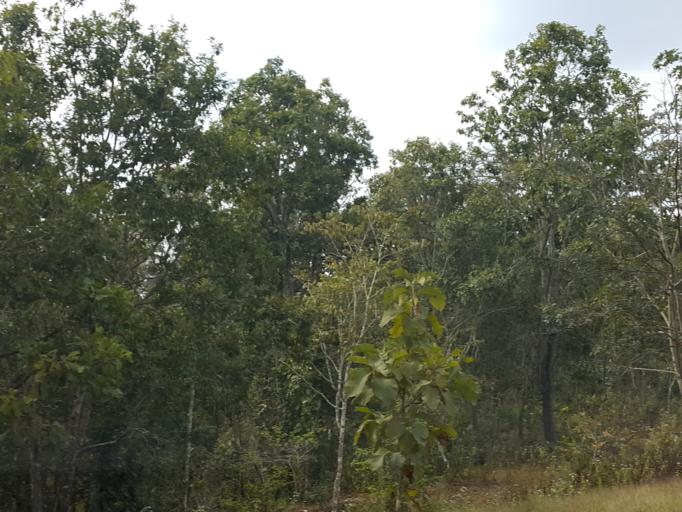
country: TH
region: Chiang Mai
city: Om Koi
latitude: 17.8460
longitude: 98.3714
